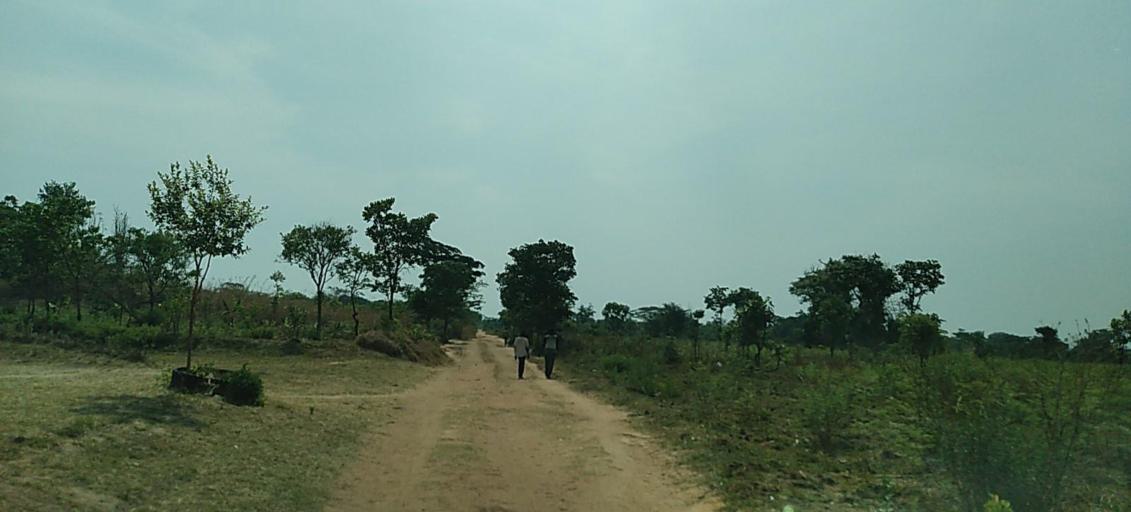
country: ZM
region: Copperbelt
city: Ndola
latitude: -13.2098
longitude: 28.7382
